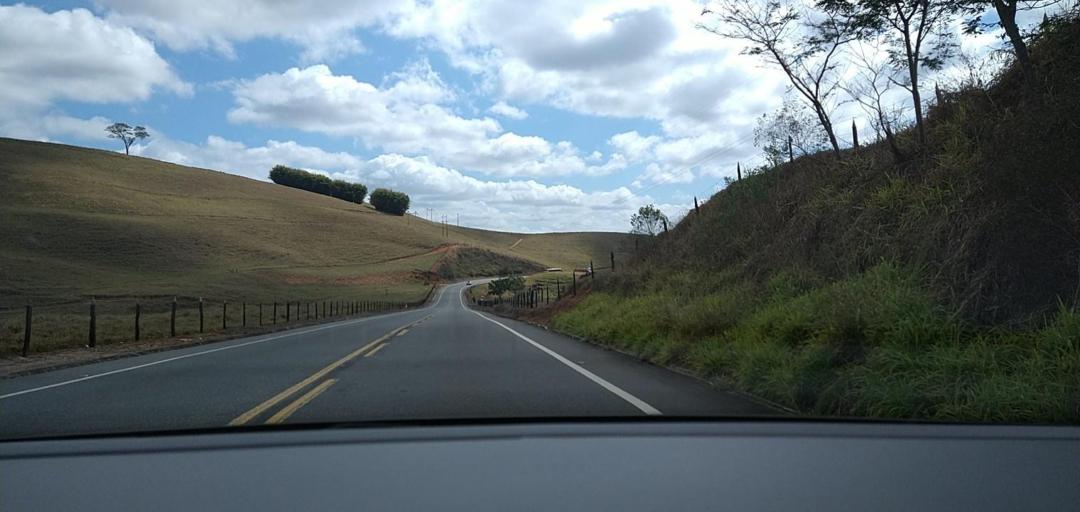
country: BR
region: Minas Gerais
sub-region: Ponte Nova
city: Ponte Nova
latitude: -20.4926
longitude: -42.8796
